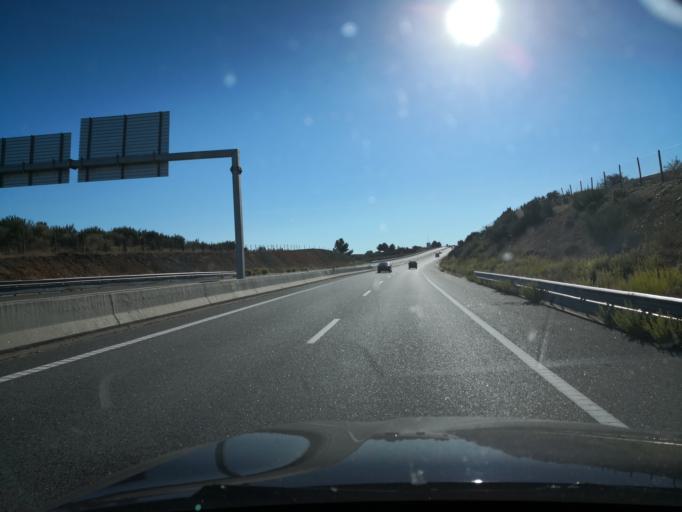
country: PT
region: Braganca
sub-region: Mirandela
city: Mirandela
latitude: 41.4477
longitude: -7.2928
